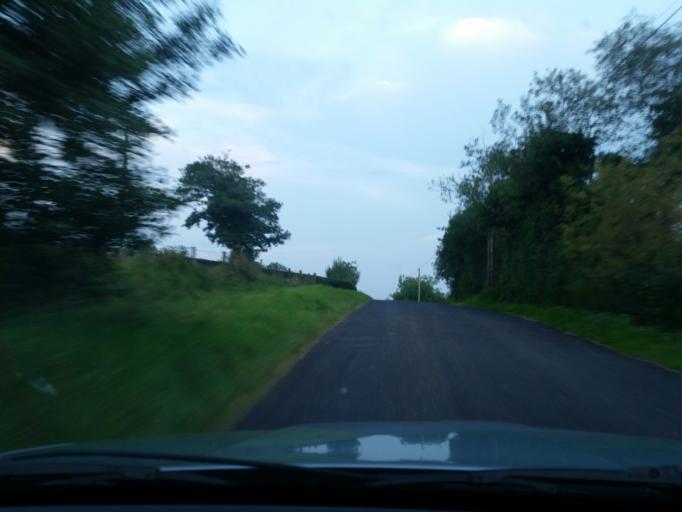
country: GB
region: Northern Ireland
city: Fivemiletown
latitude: 54.3067
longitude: -7.2952
